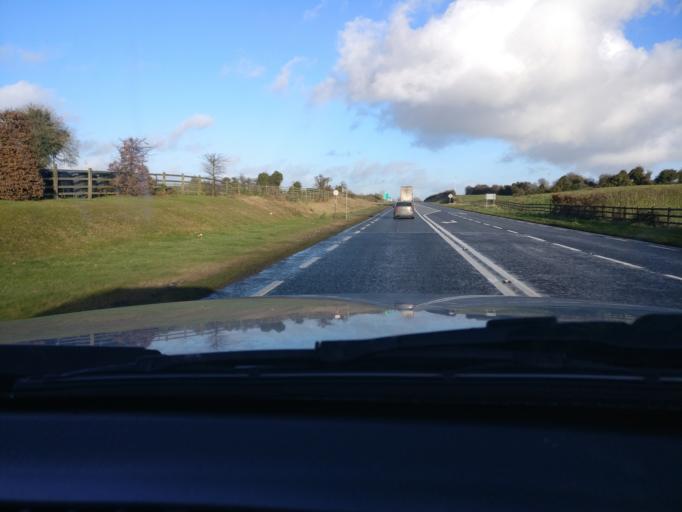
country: IE
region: Leinster
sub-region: An Iarmhi
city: Rathwire
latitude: 53.5961
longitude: -7.1129
